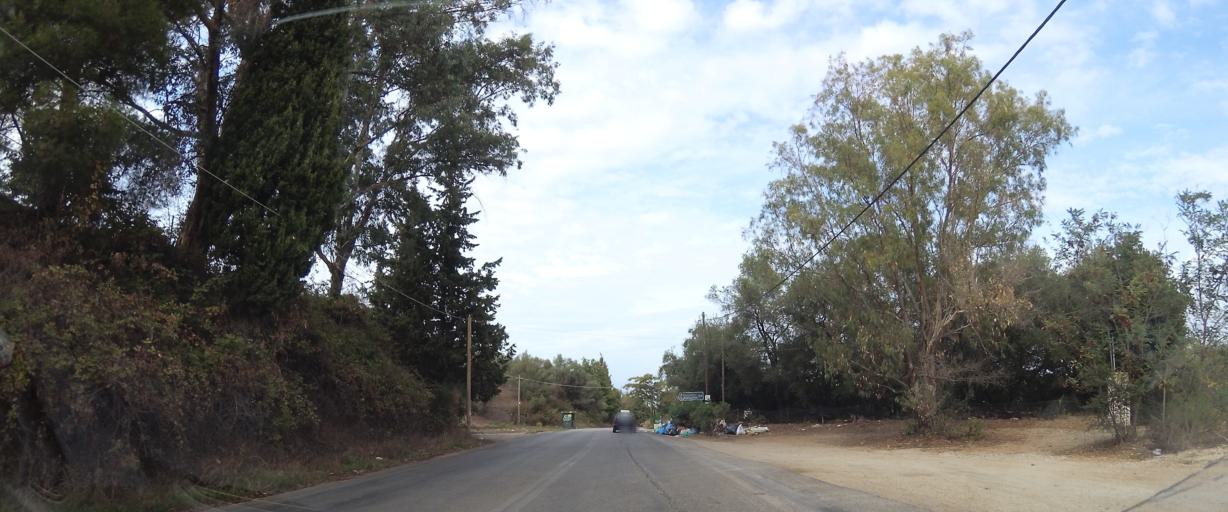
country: GR
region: Ionian Islands
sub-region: Nomos Kerkyras
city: Acharavi
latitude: 39.7618
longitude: 19.9324
